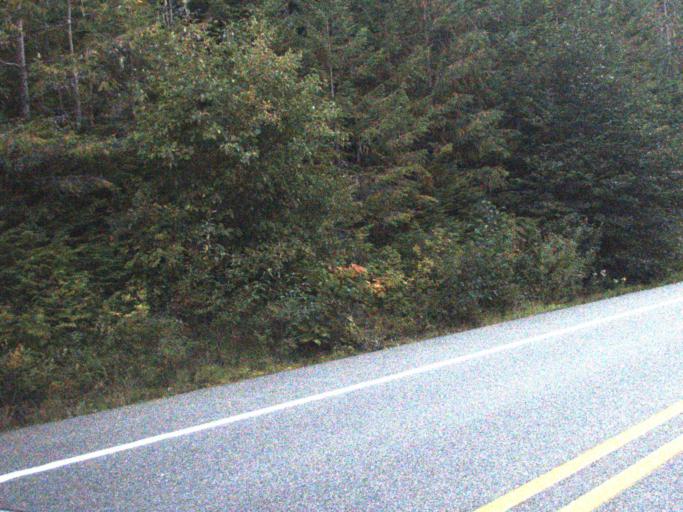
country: US
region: Washington
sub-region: Snohomish County
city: Darrington
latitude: 48.6686
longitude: -120.8746
